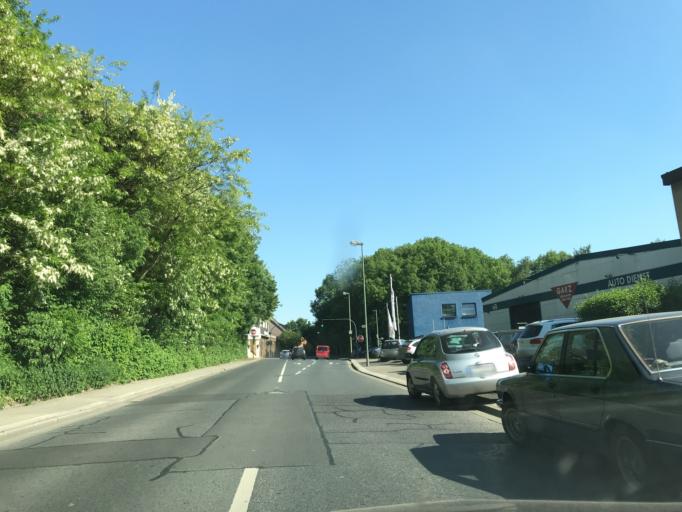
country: DE
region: North Rhine-Westphalia
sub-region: Regierungsbezirk Dusseldorf
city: Essen
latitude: 51.4720
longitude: 7.0686
